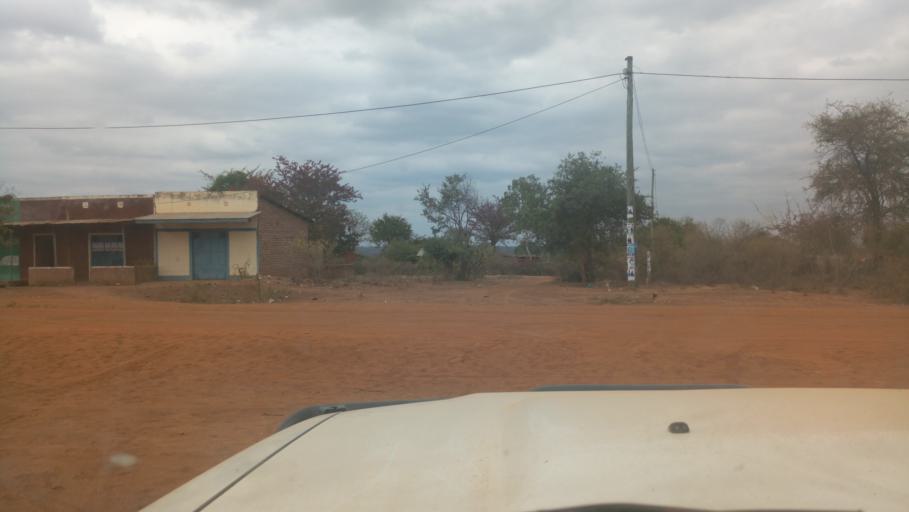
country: KE
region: Kitui
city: Kitui
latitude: -1.5978
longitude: 37.9148
